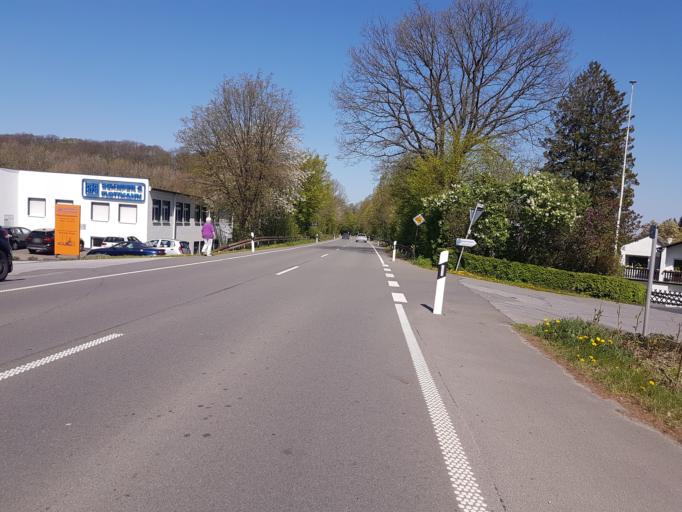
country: DE
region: North Rhine-Westphalia
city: Gevelsberg
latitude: 51.3618
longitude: 7.3293
